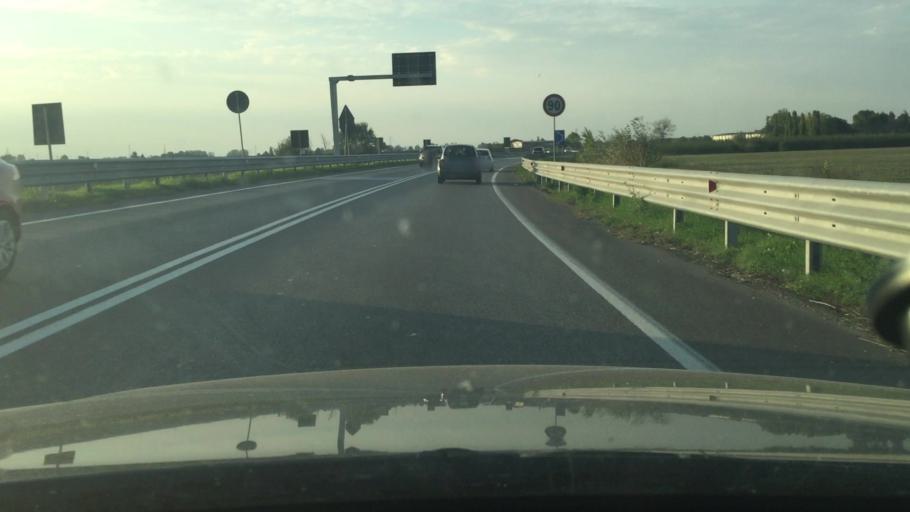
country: IT
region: Emilia-Romagna
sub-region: Provincia di Ferrara
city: Ferrara
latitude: 44.8272
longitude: 11.5828
